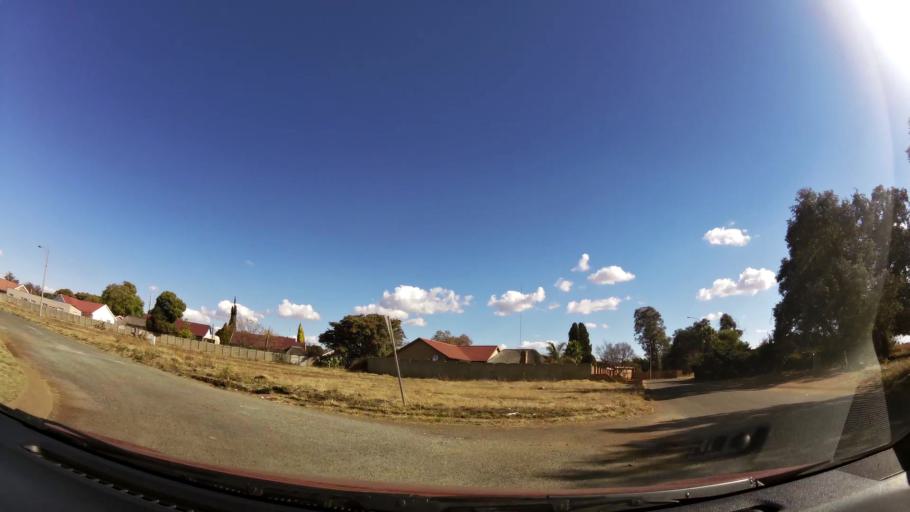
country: ZA
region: Gauteng
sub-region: West Rand District Municipality
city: Carletonville
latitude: -26.3581
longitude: 27.3717
